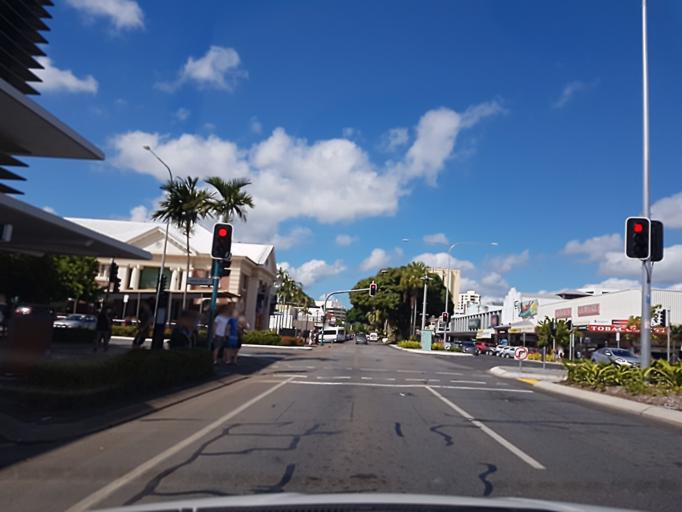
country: AU
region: Queensland
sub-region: Cairns
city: Cairns
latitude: -16.9210
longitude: 145.7766
